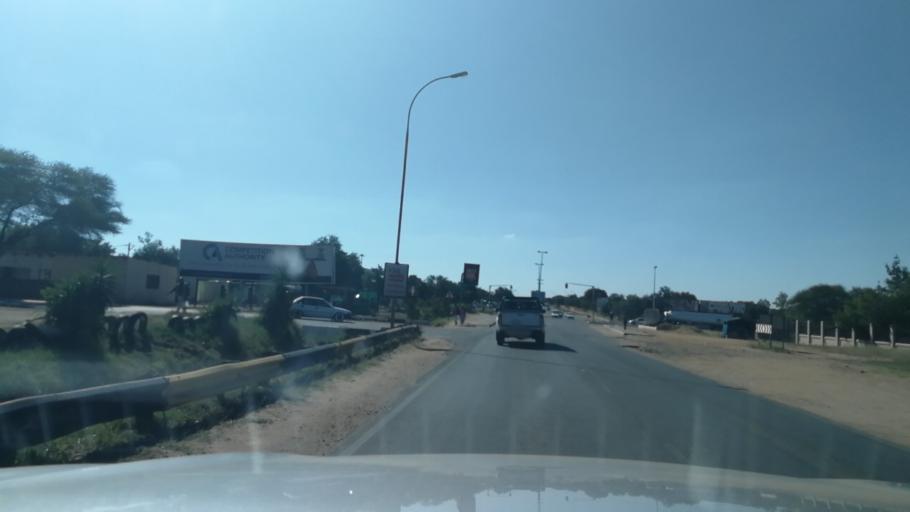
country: BW
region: South East
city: Gaborone
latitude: -24.6825
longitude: 25.9059
